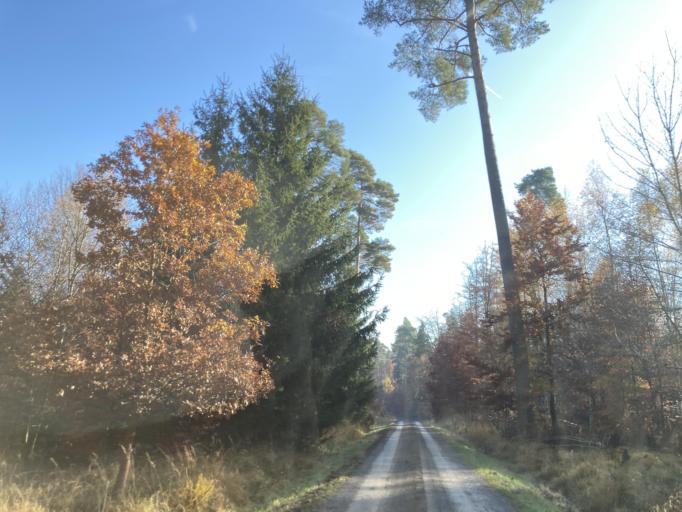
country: DE
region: Baden-Wuerttemberg
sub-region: Regierungsbezirk Stuttgart
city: Altdorf
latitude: 48.5747
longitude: 9.0012
